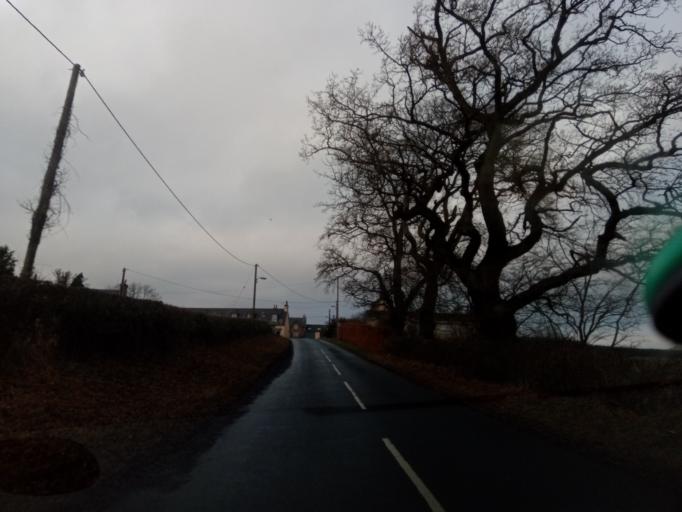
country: GB
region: Scotland
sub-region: The Scottish Borders
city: Saint Boswells
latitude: 55.5840
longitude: -2.6149
